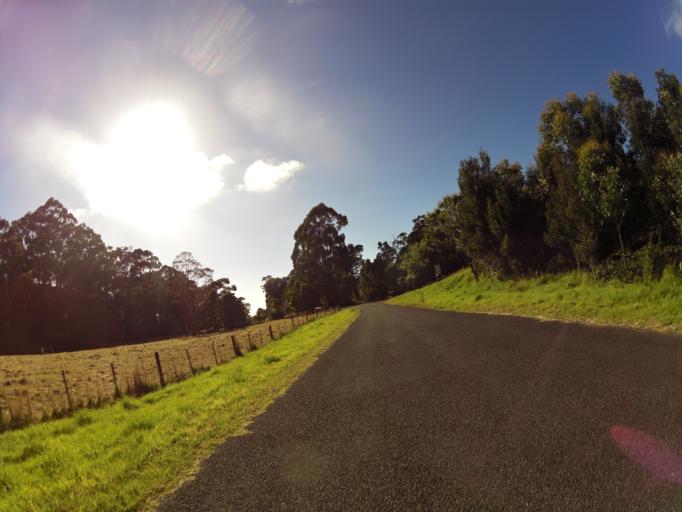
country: AU
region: Victoria
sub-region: Colac-Otway
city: Apollo Bay
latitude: -38.7645
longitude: 143.6324
